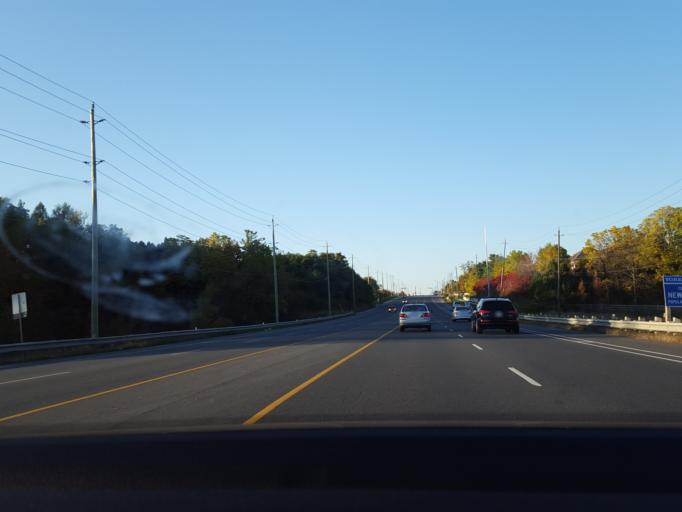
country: CA
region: Ontario
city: Newmarket
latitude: 44.0218
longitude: -79.4727
